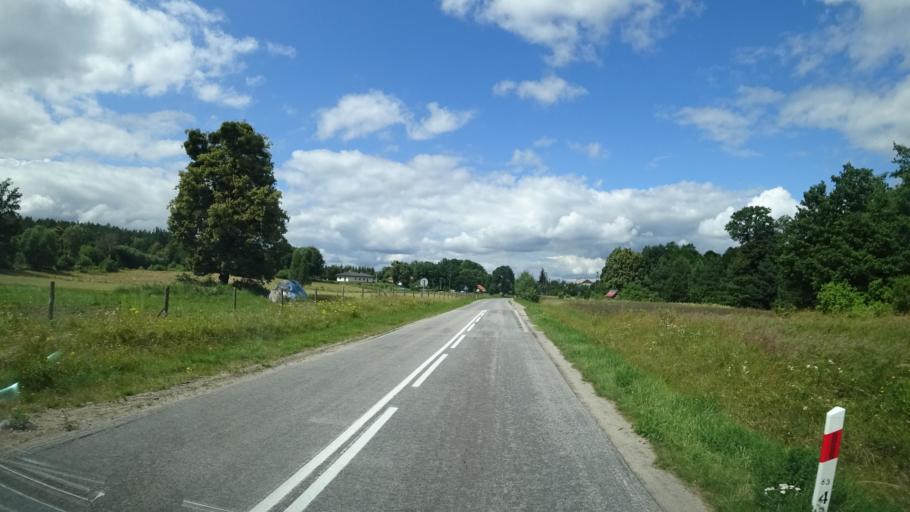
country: PL
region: Warmian-Masurian Voivodeship
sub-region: Powiat goldapski
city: Banie Mazurskie
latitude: 54.2151
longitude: 22.1574
